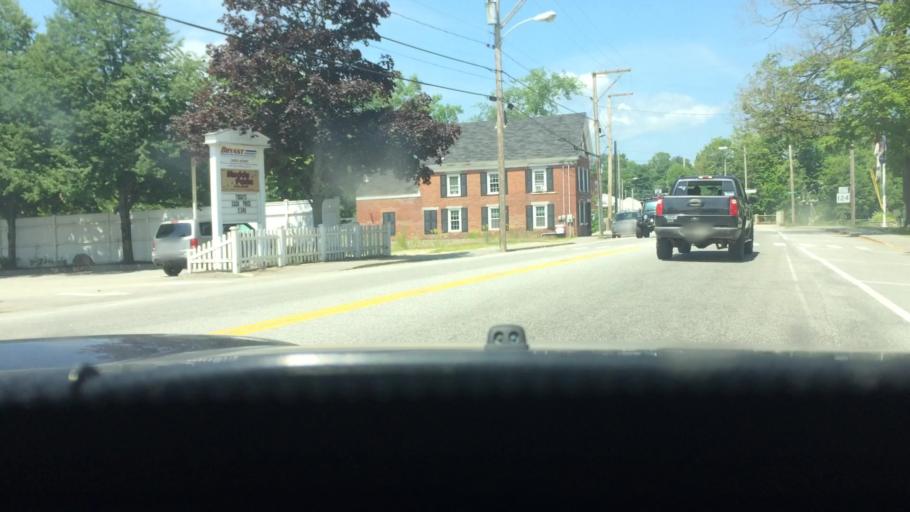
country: US
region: Maine
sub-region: Androscoggin County
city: Mechanic Falls
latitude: 44.1105
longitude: -70.3899
